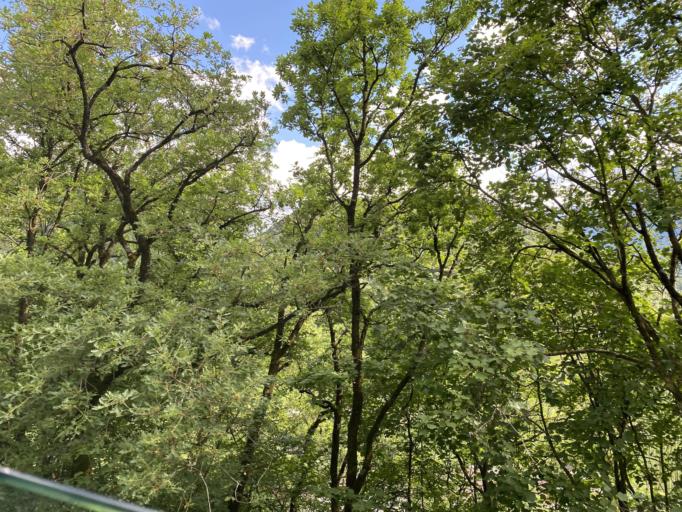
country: CH
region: Vaud
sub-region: Aigle District
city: Aigle
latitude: 46.3183
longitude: 6.9812
